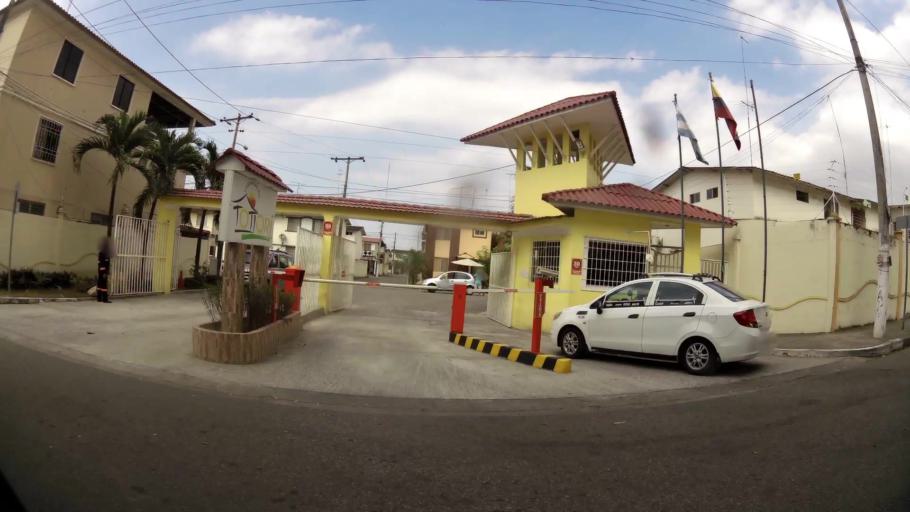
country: EC
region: Guayas
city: Santa Lucia
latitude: -2.0864
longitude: -79.9405
